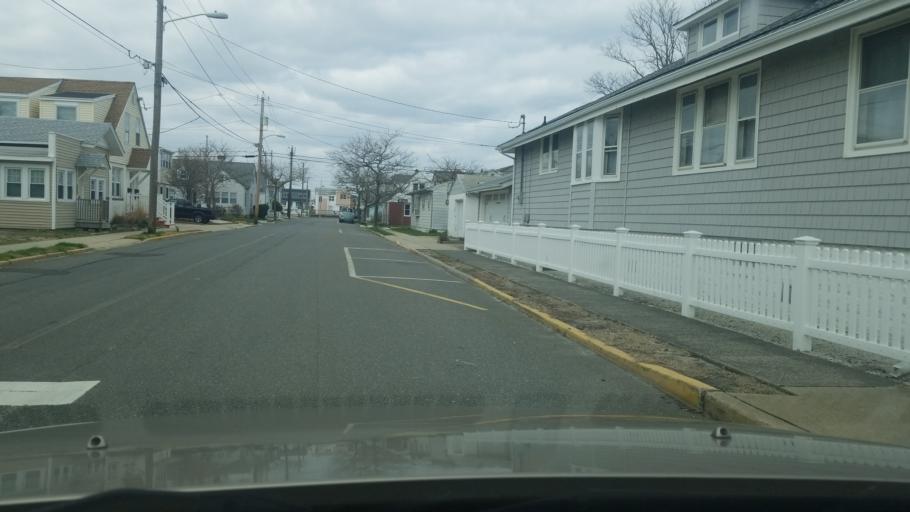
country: US
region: New Jersey
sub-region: Ocean County
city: Seaside Heights
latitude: 39.9417
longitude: -74.0773
